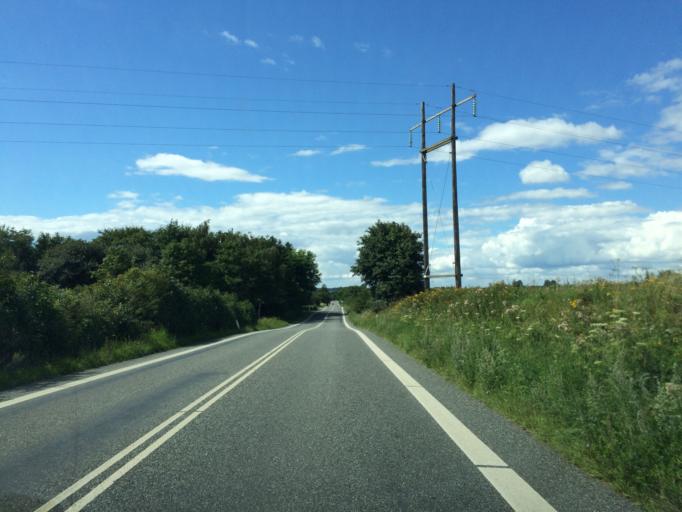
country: DK
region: South Denmark
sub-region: Faaborg-Midtfyn Kommune
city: Faaborg
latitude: 55.1381
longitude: 10.1770
